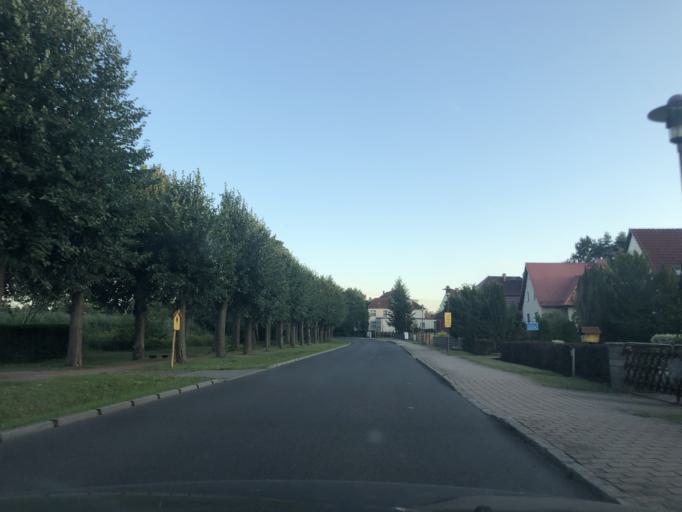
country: DE
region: Brandenburg
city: Mullrose
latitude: 52.2385
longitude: 14.4123
